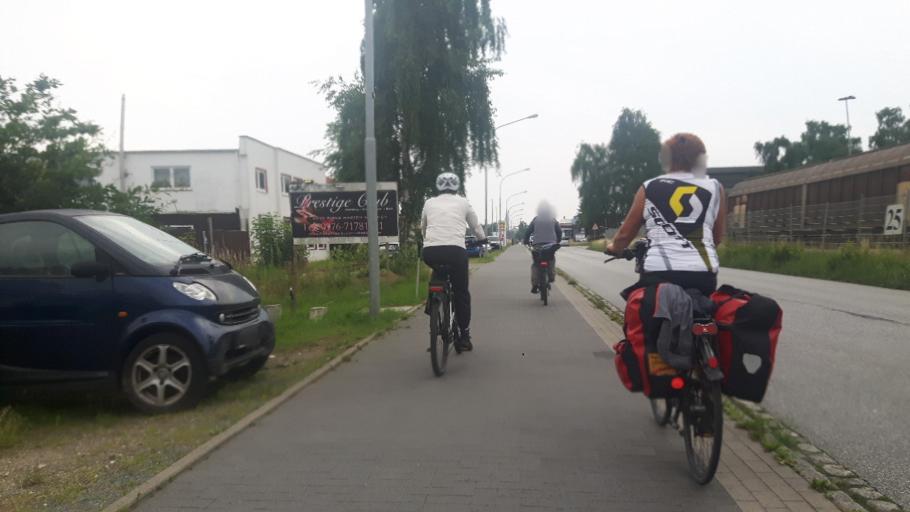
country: DE
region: Schleswig-Holstein
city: Luebeck
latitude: 53.8921
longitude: 10.6924
